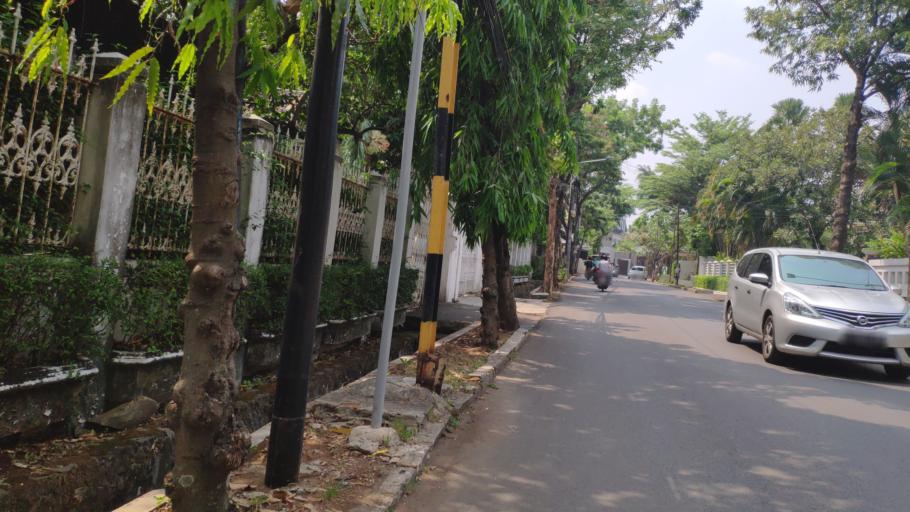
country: ID
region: West Java
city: Pamulang
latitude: -6.2964
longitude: 106.7995
